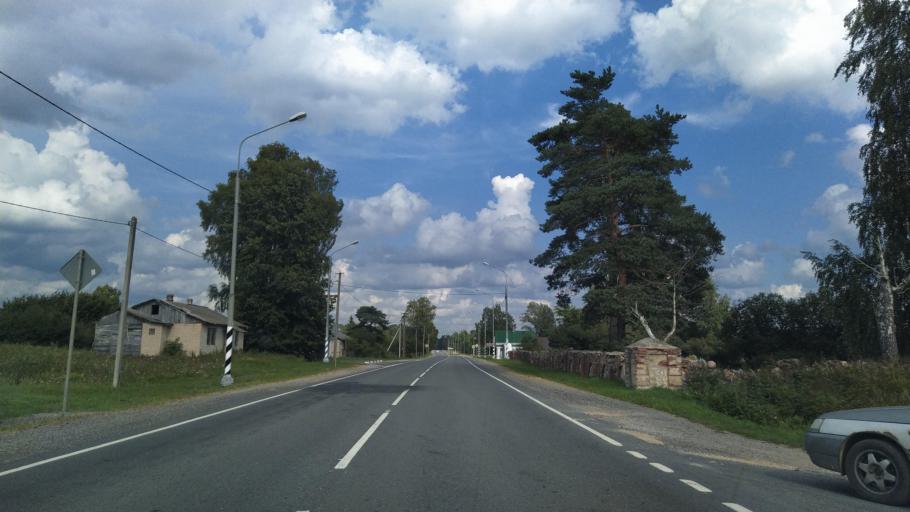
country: RU
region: Novgorod
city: Sol'tsy
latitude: 58.1014
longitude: 30.1991
